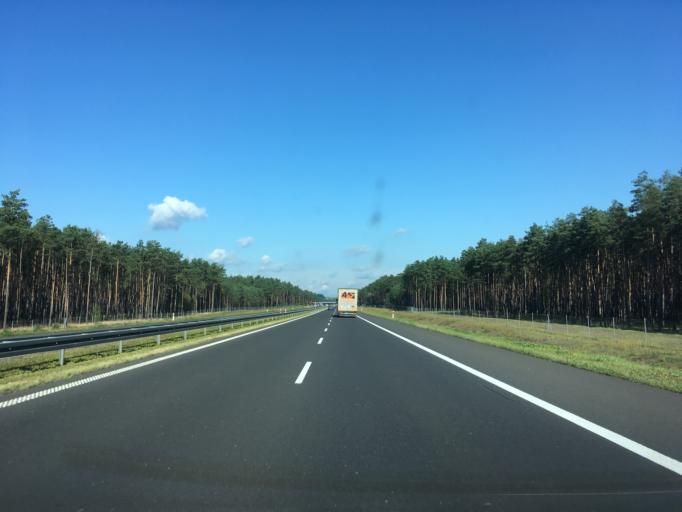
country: PL
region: Kujawsko-Pomorskie
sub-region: Powiat swiecki
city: Warlubie
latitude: 53.5096
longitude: 18.6078
